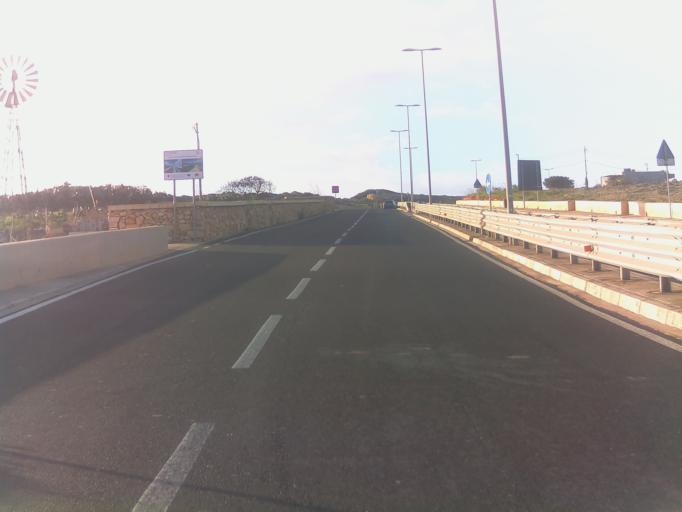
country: MT
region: Il-Mellieha
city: Mellieha
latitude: 35.9854
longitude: 14.3421
